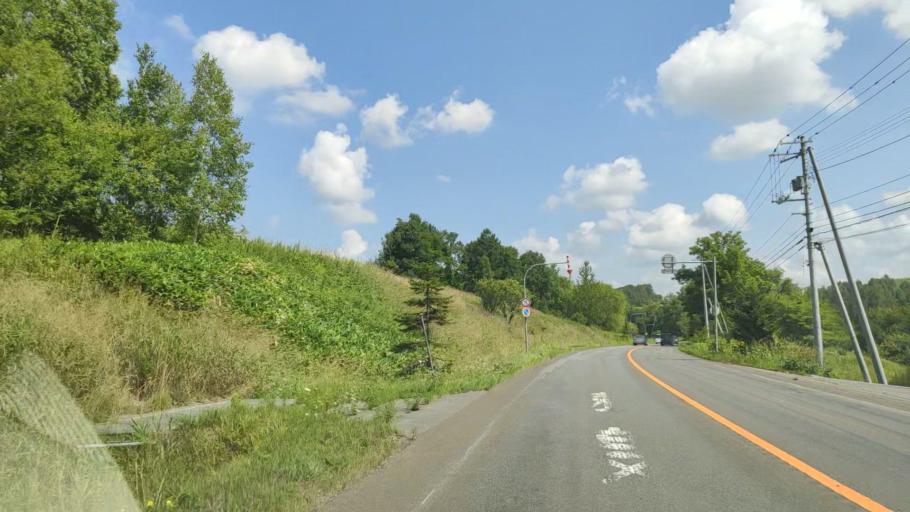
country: JP
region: Hokkaido
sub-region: Asahikawa-shi
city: Asahikawa
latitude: 43.5717
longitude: 142.4377
